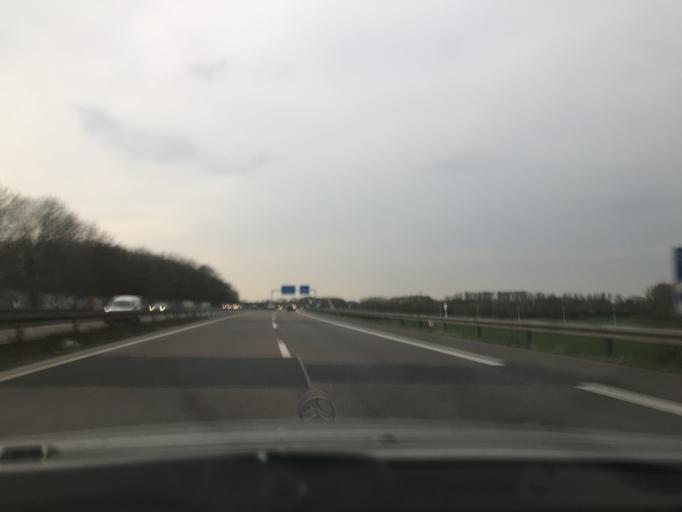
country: DE
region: North Rhine-Westphalia
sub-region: Regierungsbezirk Dusseldorf
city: Korschenbroich
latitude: 51.2346
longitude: 6.4870
